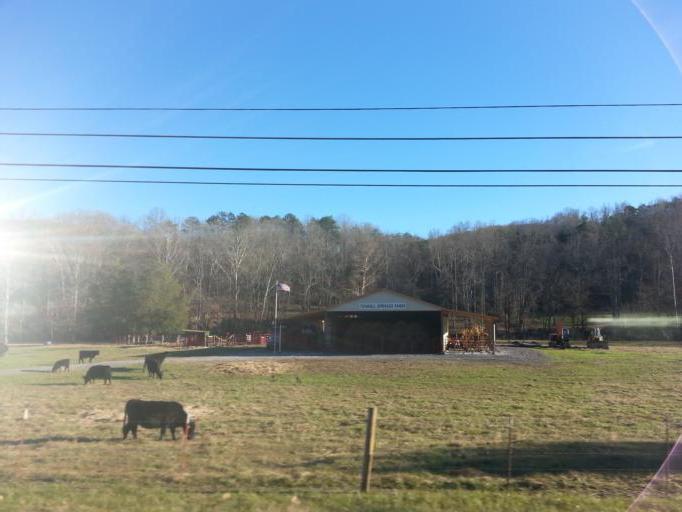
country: US
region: Tennessee
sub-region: Anderson County
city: Oak Ridge
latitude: 36.0462
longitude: -84.2488
